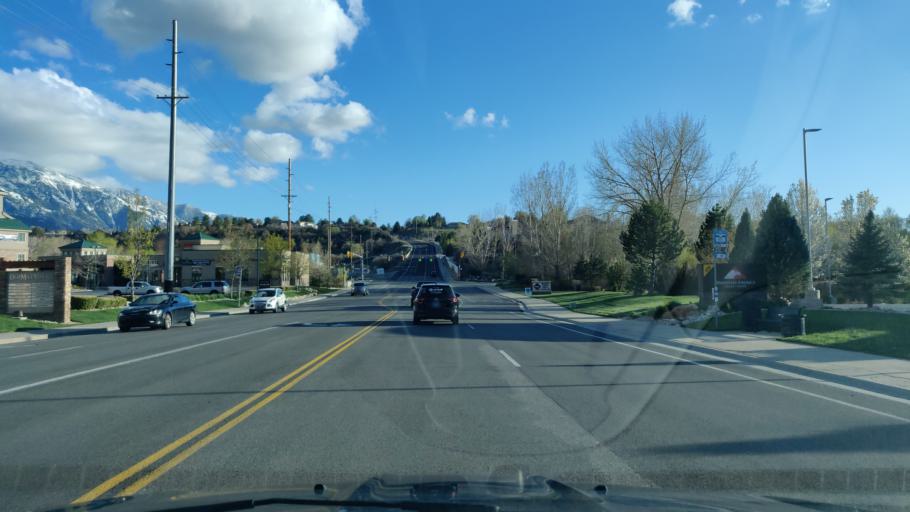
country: US
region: Utah
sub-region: Salt Lake County
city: Cottonwood Heights
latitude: 40.6332
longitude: -111.8065
